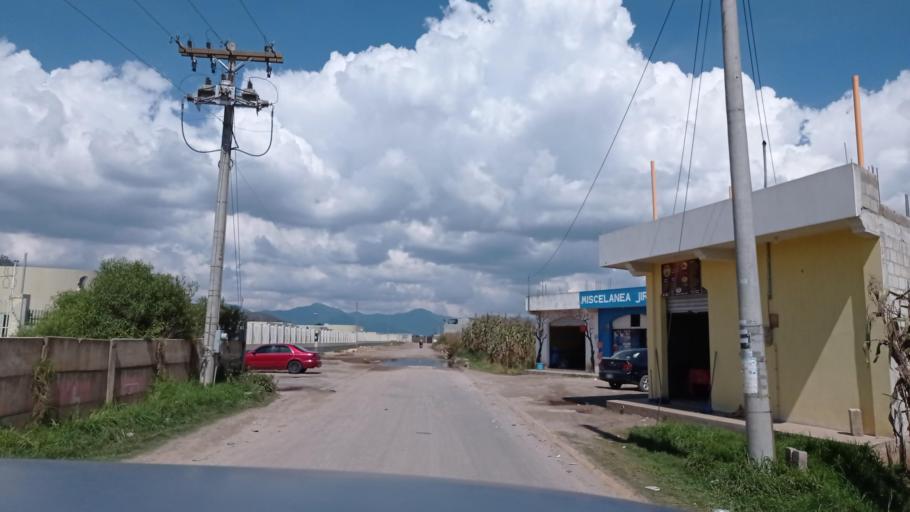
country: GT
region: Quetzaltenango
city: Olintepeque
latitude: 14.8701
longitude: -91.4938
